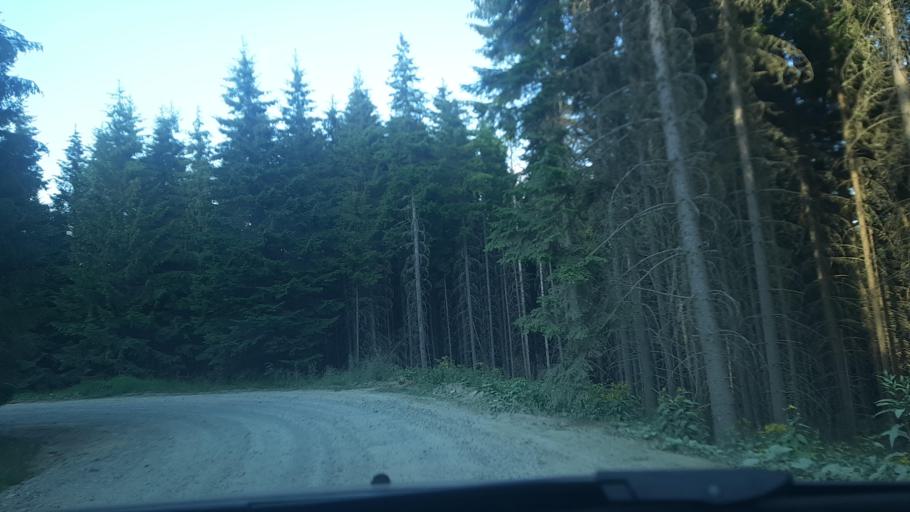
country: RO
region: Alba
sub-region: Comuna Sugag
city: Sugag
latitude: 45.5817
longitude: 23.6147
